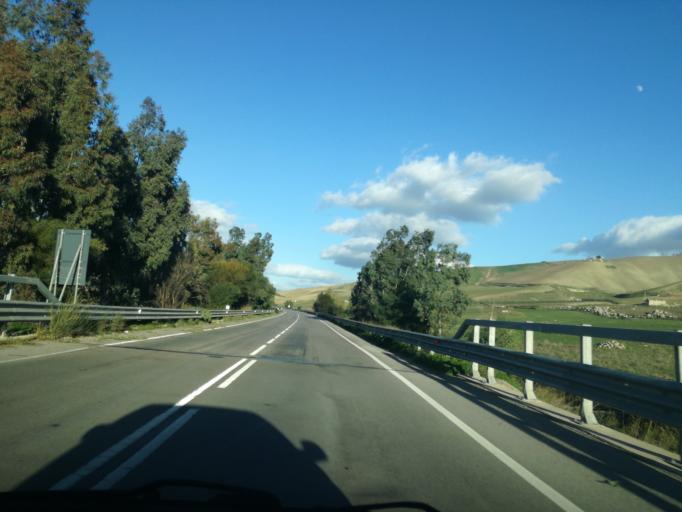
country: IT
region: Sicily
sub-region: Enna
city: Pietraperzia
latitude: 37.4345
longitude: 14.0899
